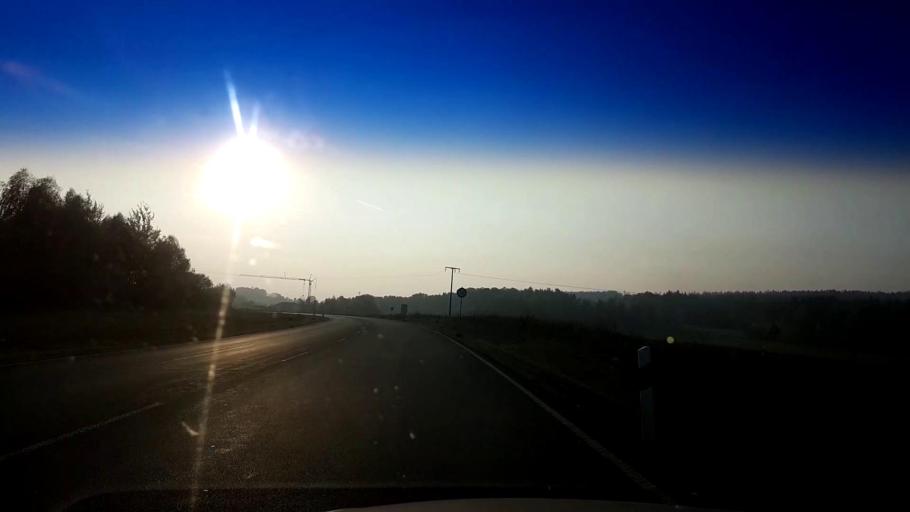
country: DE
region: Bavaria
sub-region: Upper Franconia
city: Hohenberg an der Eger
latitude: 50.0851
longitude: 12.2103
